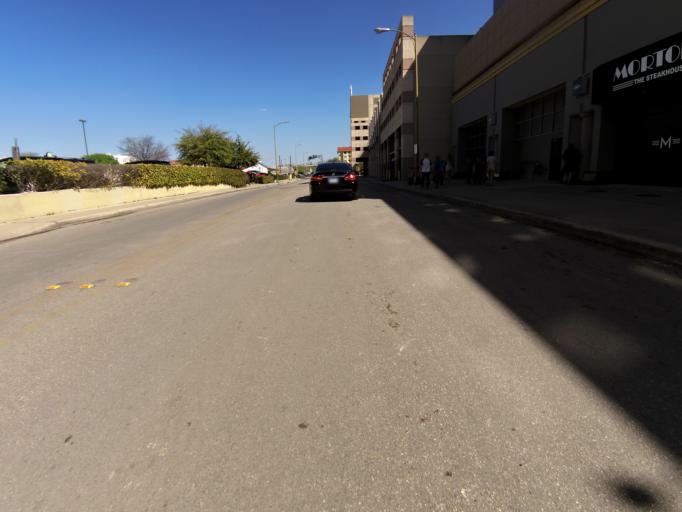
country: US
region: Texas
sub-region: Bexar County
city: San Antonio
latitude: 29.4249
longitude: -98.4850
